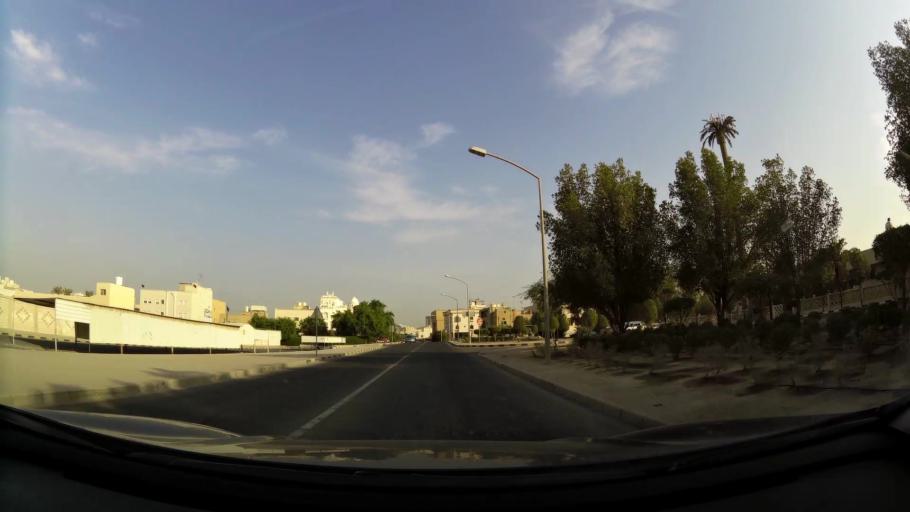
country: KW
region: Muhafazat Hawalli
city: Ar Rumaythiyah
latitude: 29.3175
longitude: 48.0730
